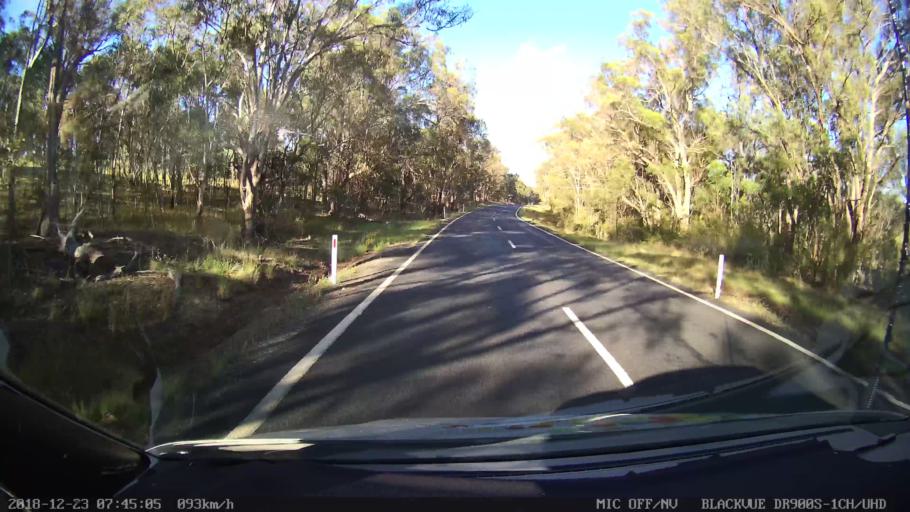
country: AU
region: New South Wales
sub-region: Armidale Dumaresq
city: Enmore
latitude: -30.5265
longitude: 151.9407
